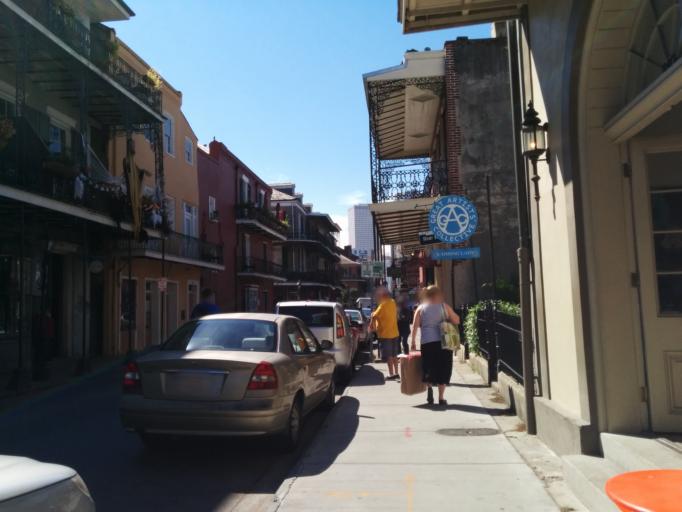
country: US
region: Louisiana
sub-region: Orleans Parish
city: New Orleans
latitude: 29.9593
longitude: -90.0636
